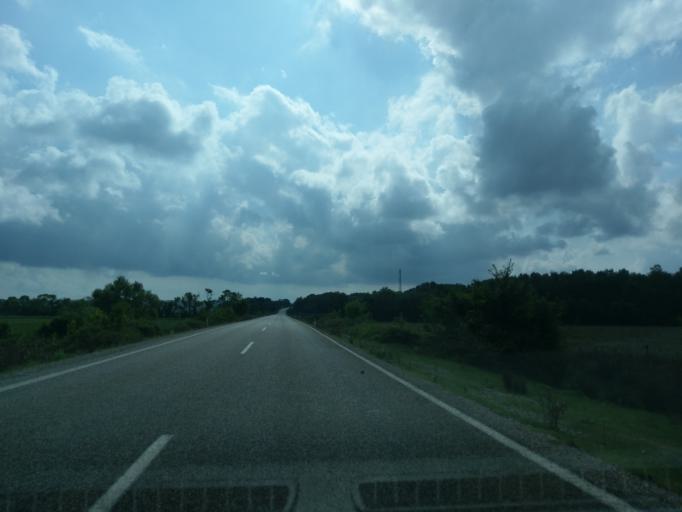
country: TR
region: Sinop
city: Sinop
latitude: 42.0261
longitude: 35.0399
